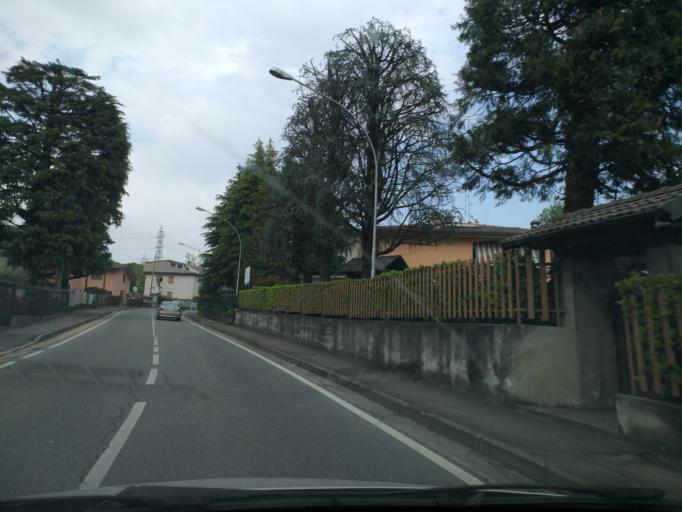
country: IT
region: Lombardy
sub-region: Provincia di Como
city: Figino Serenza
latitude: 45.7156
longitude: 9.1335
